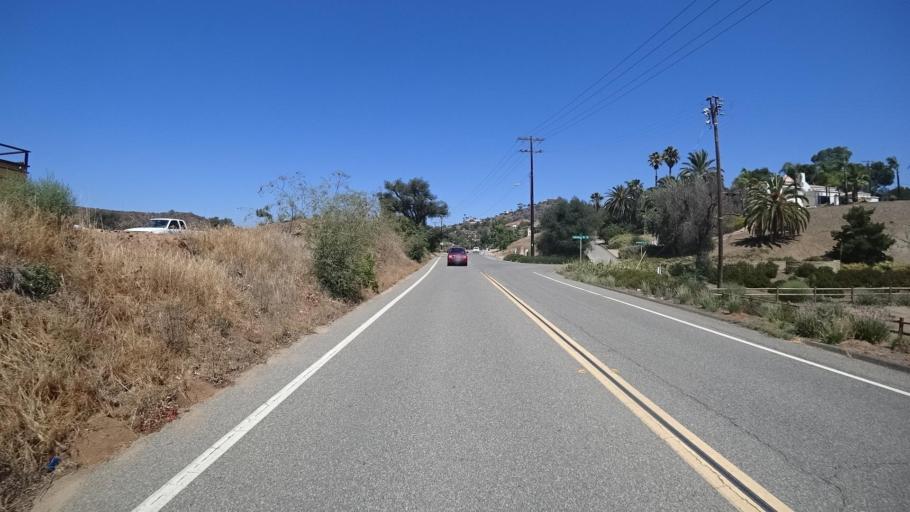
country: US
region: California
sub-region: San Diego County
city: Bonsall
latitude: 33.3412
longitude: -117.1903
